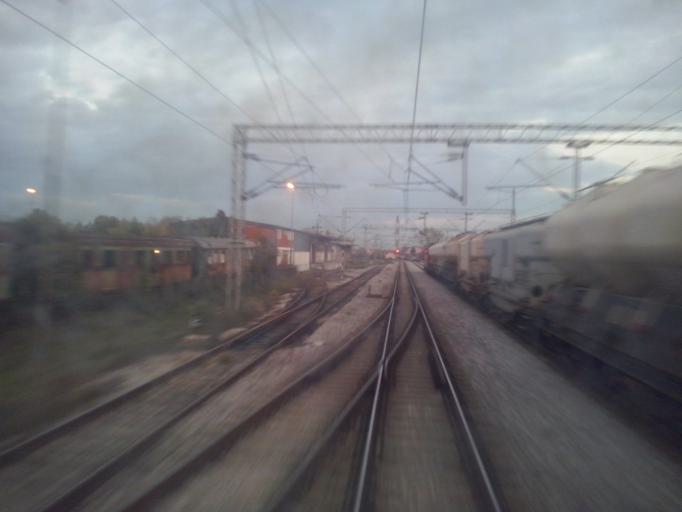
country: RS
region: Central Serbia
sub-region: Kolubarski Okrug
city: Valjevo
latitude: 44.2710
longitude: 19.9109
